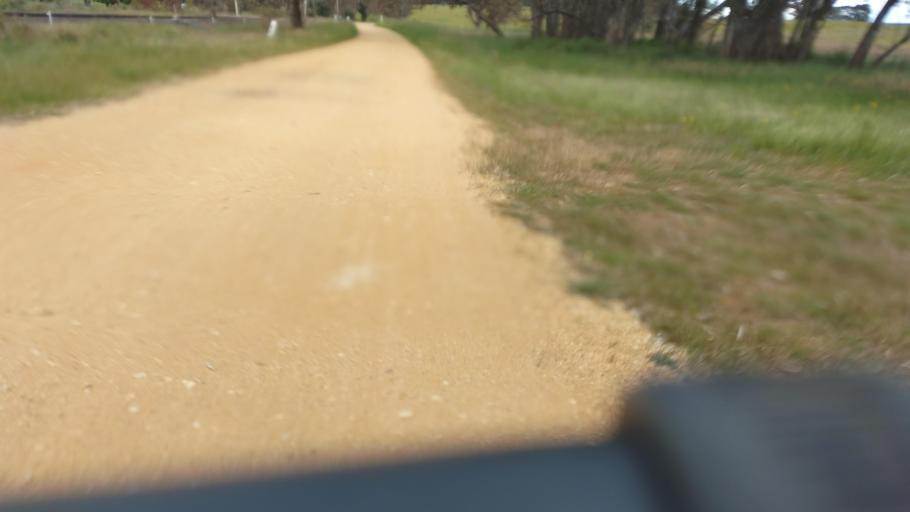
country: AU
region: Victoria
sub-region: Mount Alexander
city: Castlemaine
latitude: -37.0233
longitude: 144.1513
